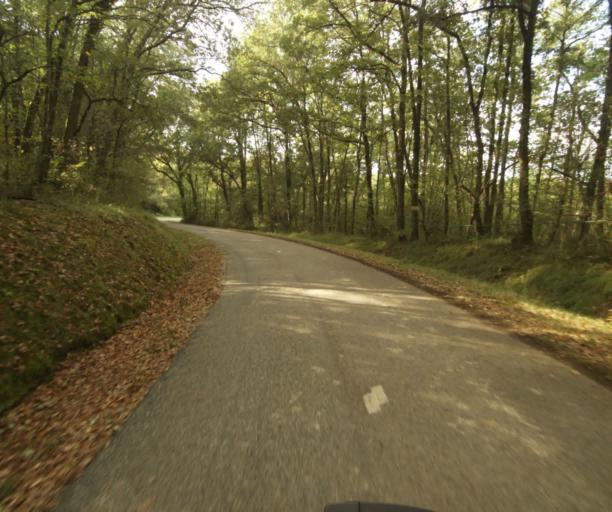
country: FR
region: Midi-Pyrenees
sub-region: Departement de la Haute-Garonne
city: Launac
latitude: 43.8336
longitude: 1.1191
